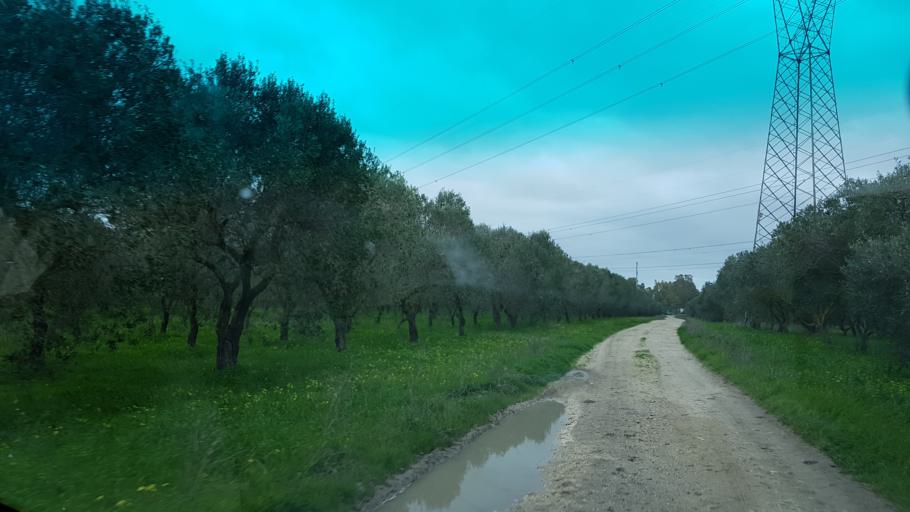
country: IT
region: Apulia
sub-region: Provincia di Brindisi
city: Tuturano
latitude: 40.5600
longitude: 17.9988
